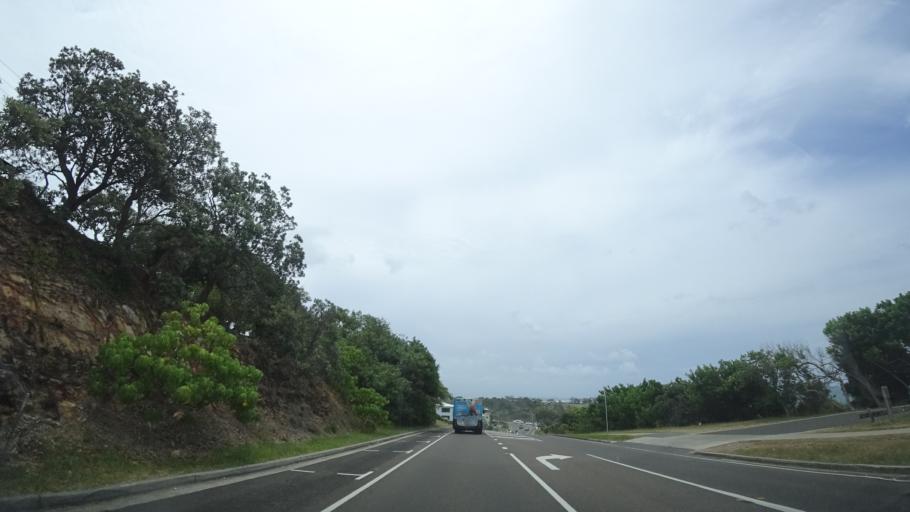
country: AU
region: Queensland
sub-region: Sunshine Coast
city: Coolum Beach
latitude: -26.5391
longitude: 153.0953
